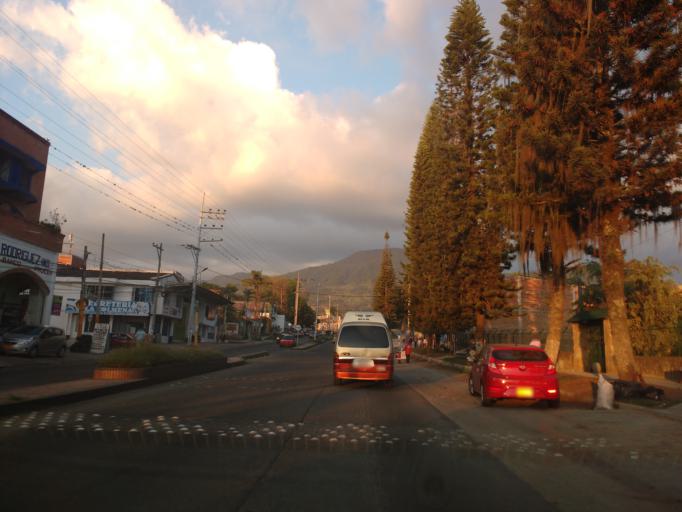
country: CO
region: Cundinamarca
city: Fusagasuga
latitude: 4.3325
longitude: -74.3726
